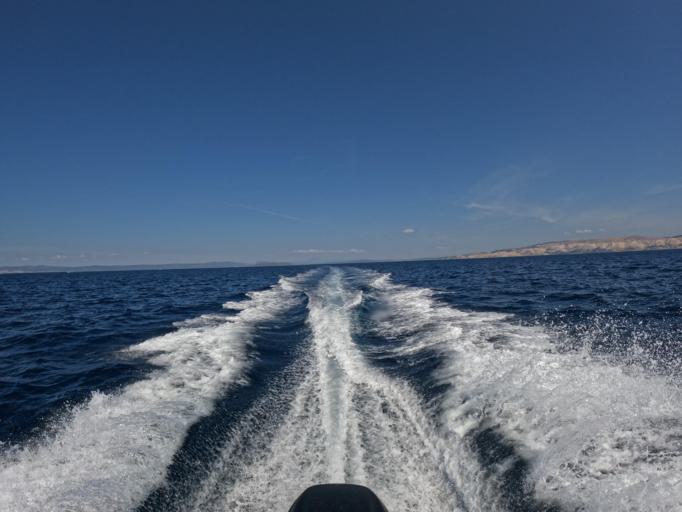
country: HR
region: Primorsko-Goranska
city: Lopar
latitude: 44.8780
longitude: 14.6602
